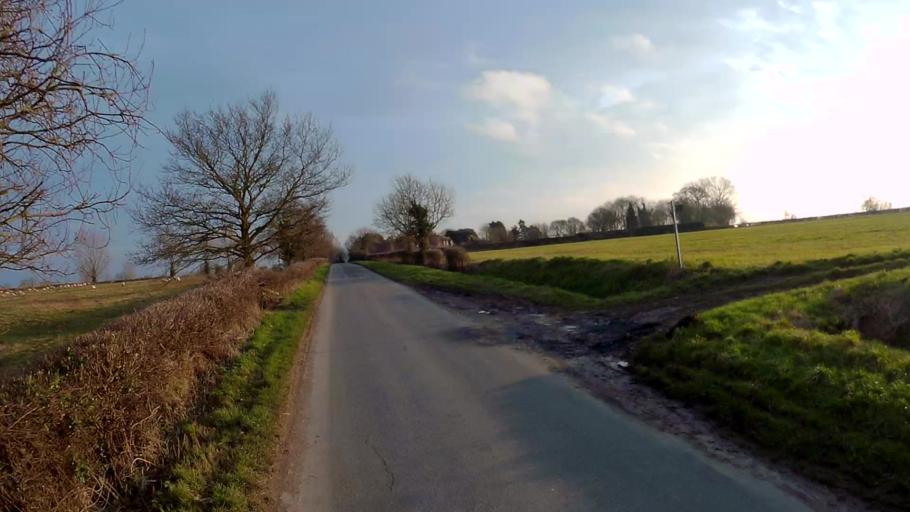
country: GB
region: England
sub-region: Lincolnshire
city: Bourne
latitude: 52.8070
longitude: -0.3958
